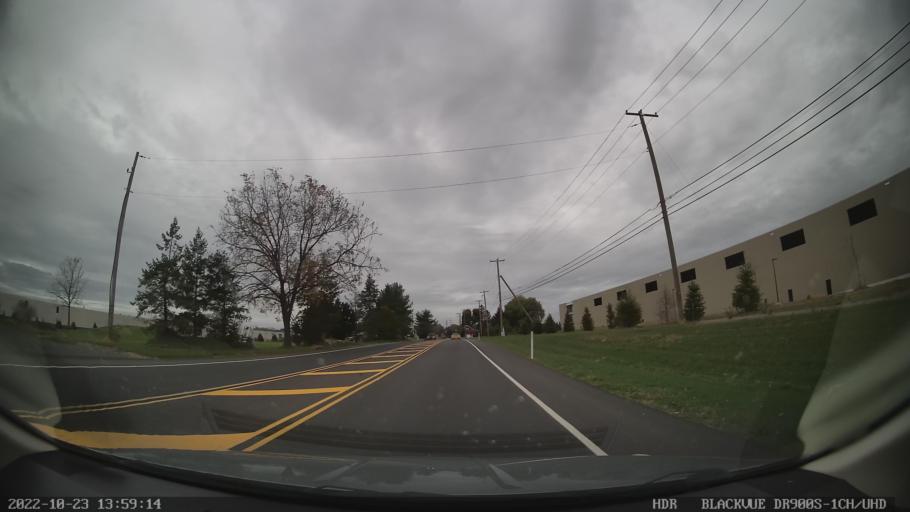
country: US
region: Pennsylvania
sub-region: Northampton County
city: Northampton
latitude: 40.7048
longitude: -75.4748
